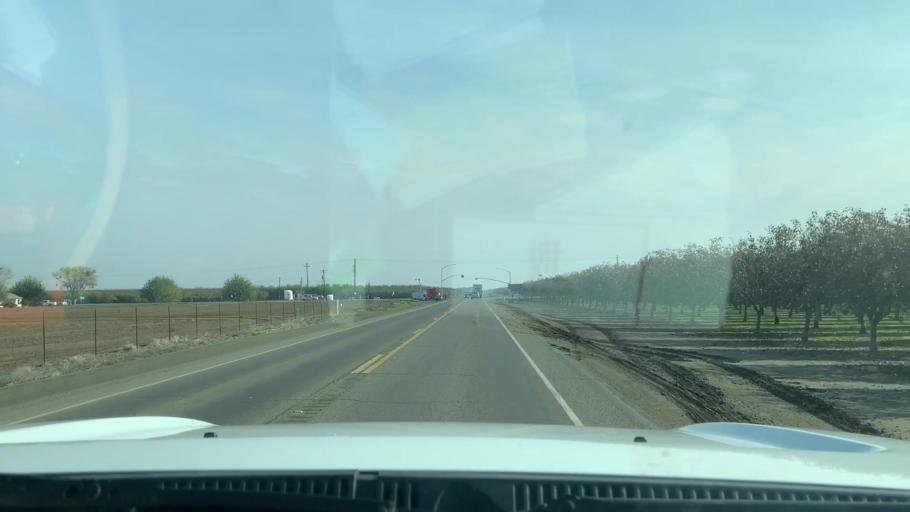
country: US
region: California
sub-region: Fresno County
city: Huron
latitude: 36.2553
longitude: -120.1064
